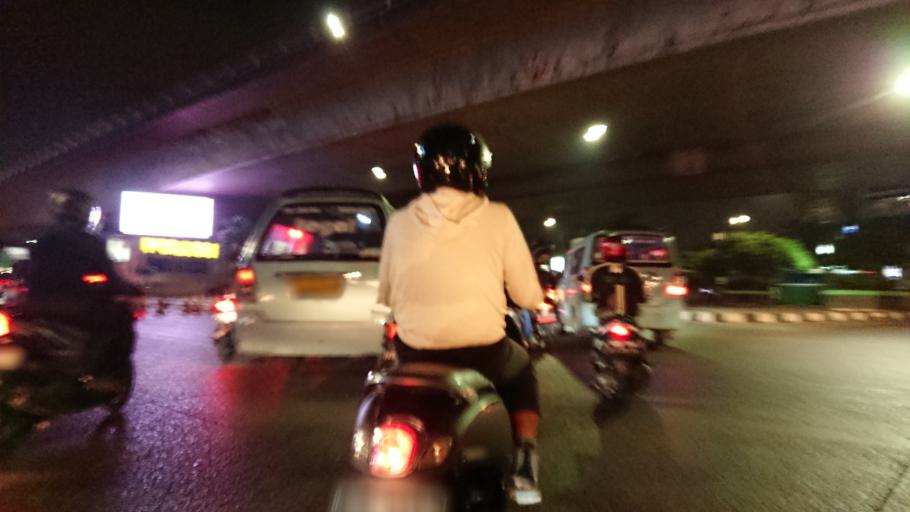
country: ID
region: Jakarta Raya
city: Jakarta
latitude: -6.2018
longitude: 106.7994
